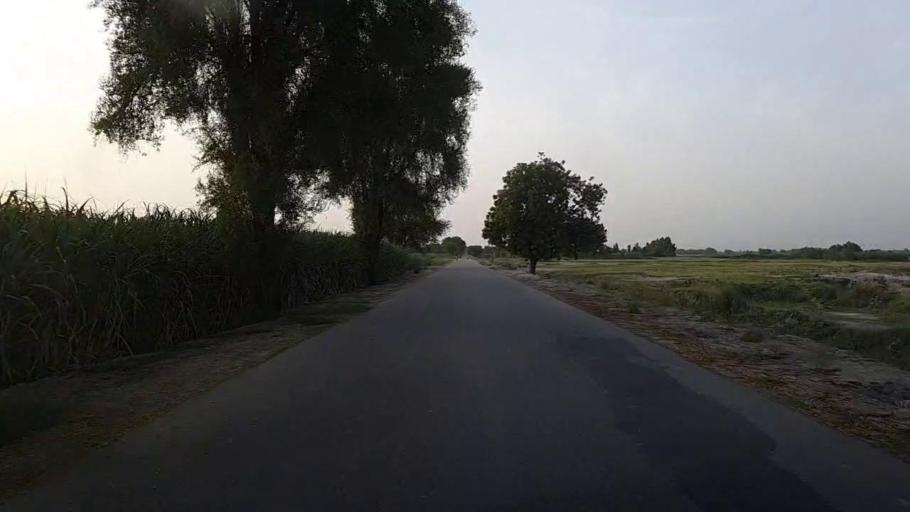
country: PK
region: Sindh
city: Ubauro
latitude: 28.2495
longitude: 69.8083
